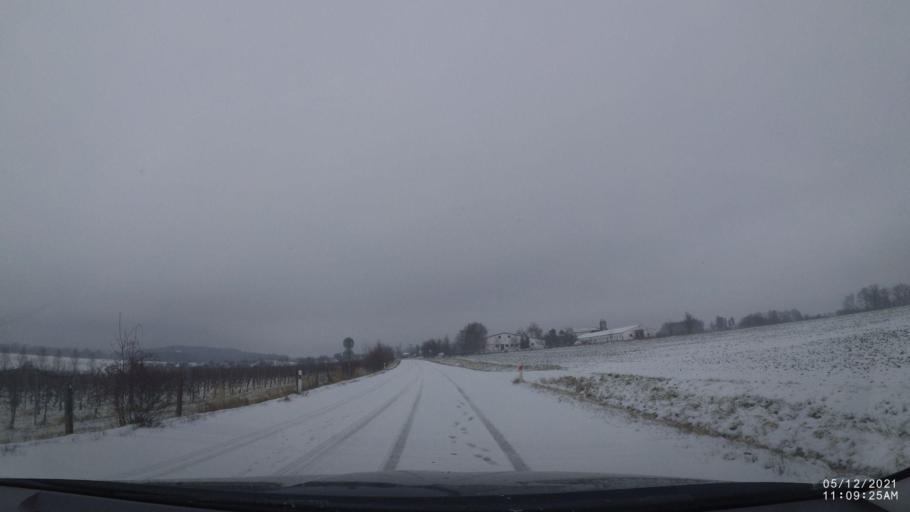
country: CZ
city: Solnice
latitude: 50.1737
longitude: 16.2228
